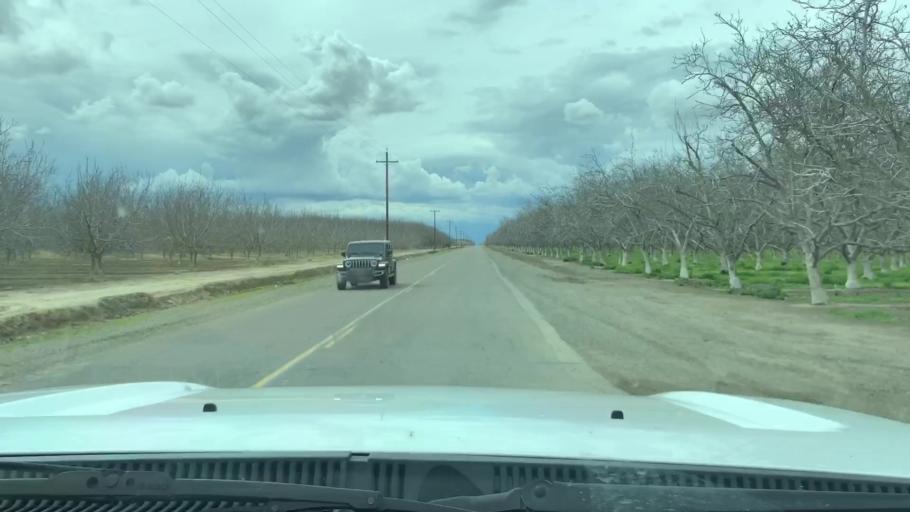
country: US
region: California
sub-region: Fresno County
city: Laton
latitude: 36.4894
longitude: -119.7555
